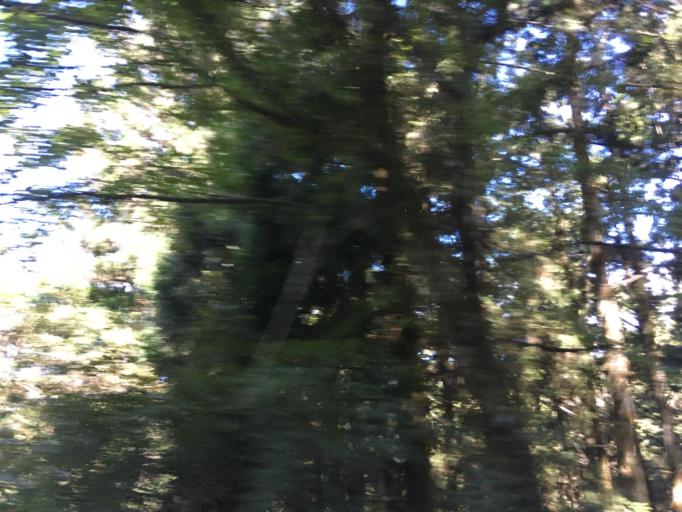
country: TW
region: Taiwan
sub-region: Yilan
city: Yilan
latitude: 24.5146
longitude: 121.5217
